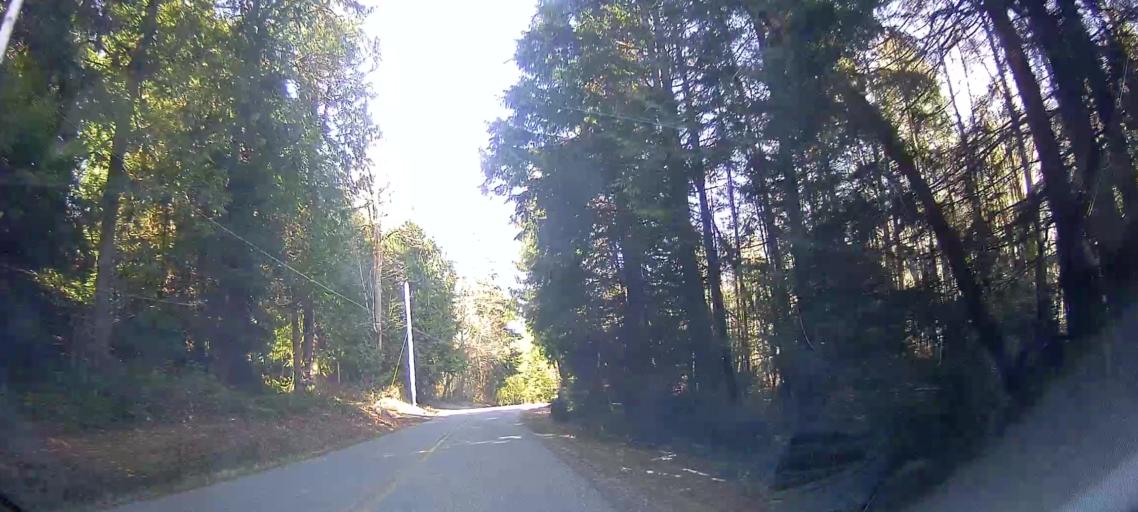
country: US
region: Washington
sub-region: Whatcom County
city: Sudden Valley
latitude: 48.6119
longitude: -122.3668
